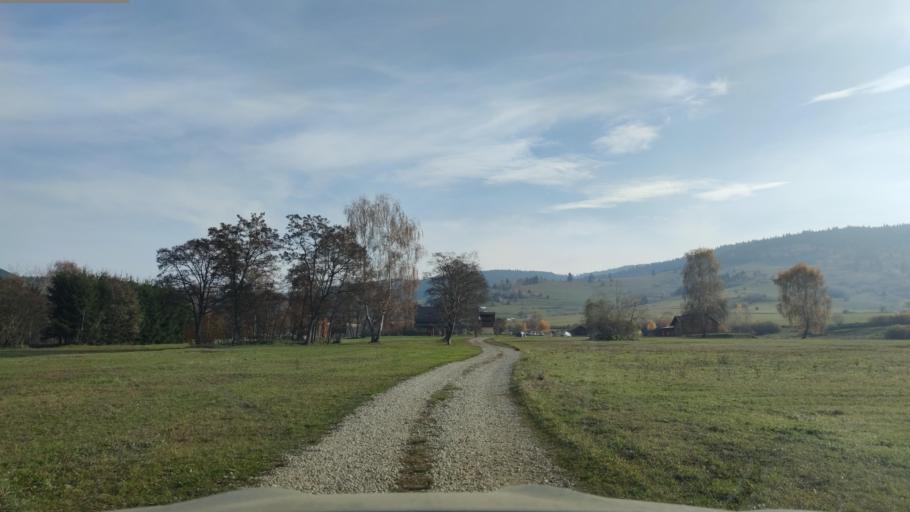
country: RO
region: Harghita
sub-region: Comuna Ditrau
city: Ditrau
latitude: 46.8211
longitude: 25.5383
